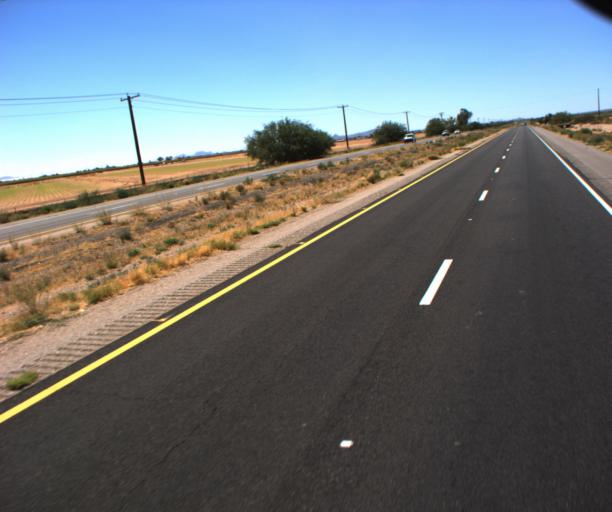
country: US
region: Arizona
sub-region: Pinal County
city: Maricopa
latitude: 32.9038
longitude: -112.0496
